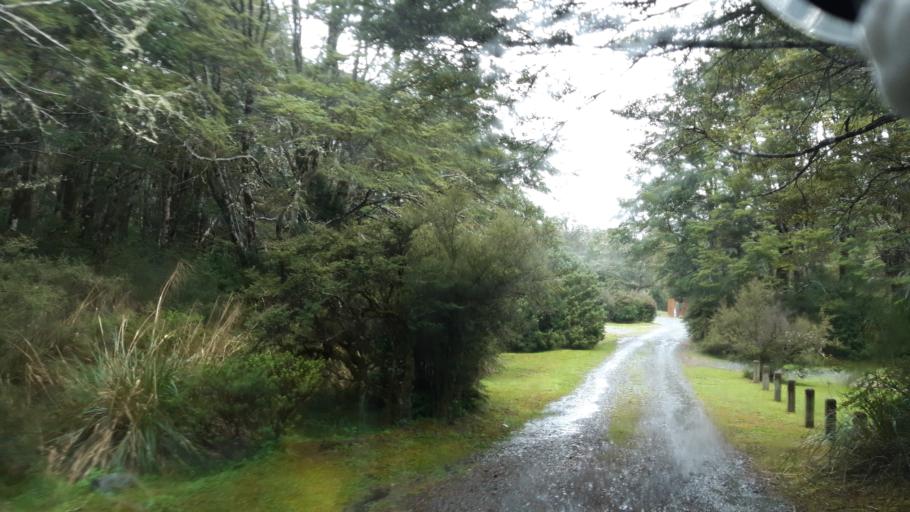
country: NZ
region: Canterbury
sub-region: Hurunui District
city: Amberley
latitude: -42.4039
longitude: 172.3970
